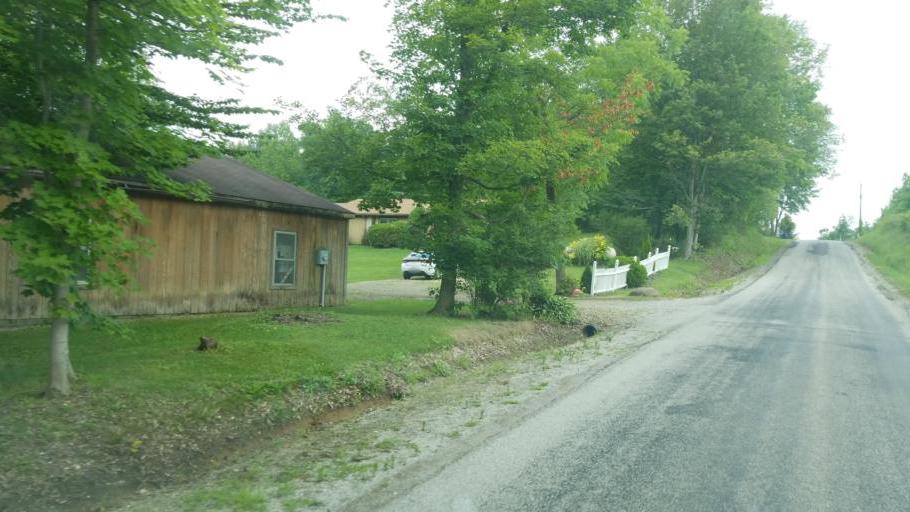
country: US
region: Ohio
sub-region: Knox County
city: Centerburg
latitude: 40.2906
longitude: -82.6259
